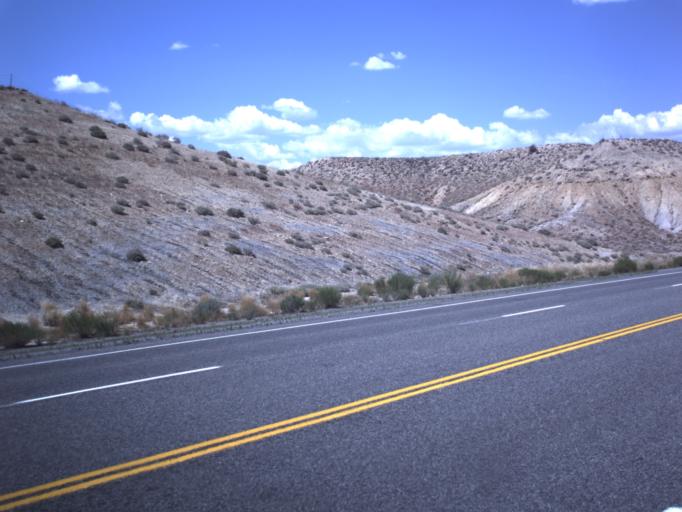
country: US
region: Utah
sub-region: Emery County
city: Huntington
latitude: 39.3775
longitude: -110.9115
